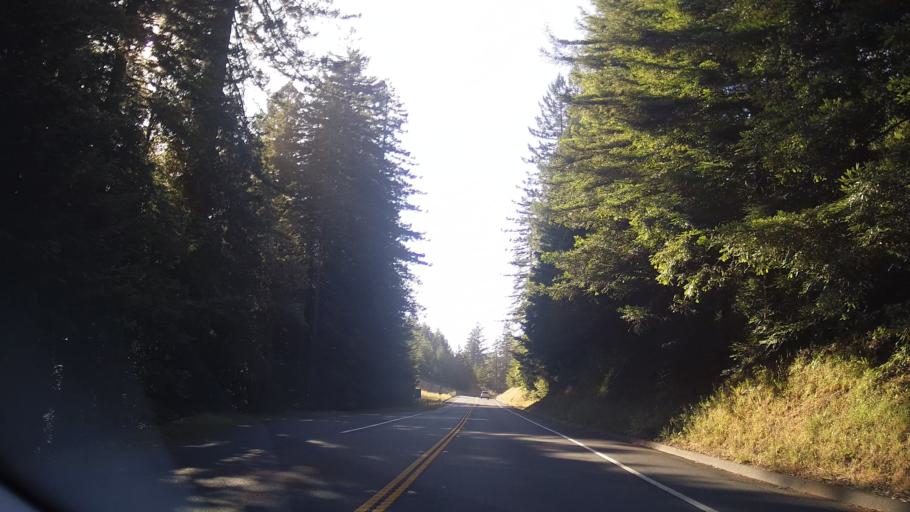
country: US
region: California
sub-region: Mendocino County
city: Fort Bragg
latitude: 39.3711
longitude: -123.6802
